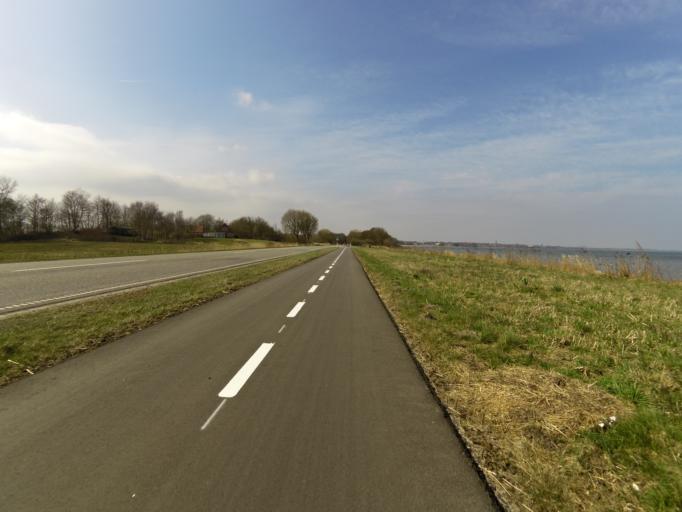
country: DK
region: Central Jutland
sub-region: Struer Kommune
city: Struer
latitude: 56.4692
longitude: 8.6371
